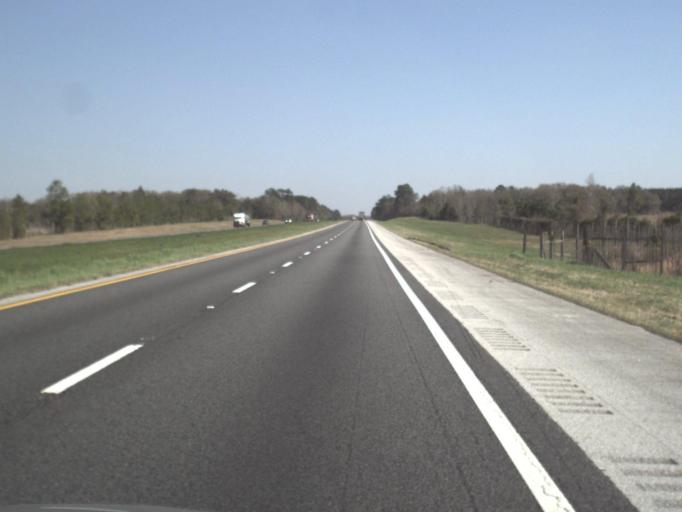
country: US
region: Florida
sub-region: Jackson County
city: Marianna
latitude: 30.6835
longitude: -85.1028
